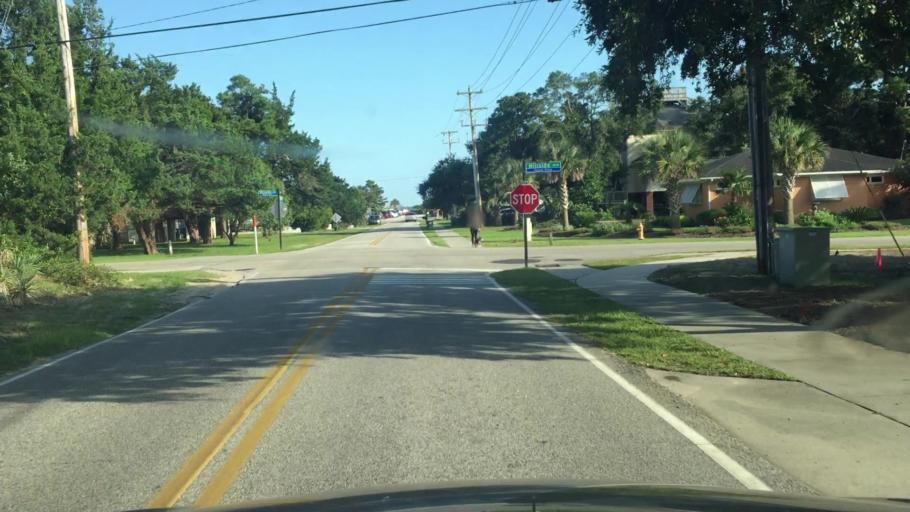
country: US
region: South Carolina
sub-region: Horry County
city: North Myrtle Beach
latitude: 33.8238
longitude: -78.6639
